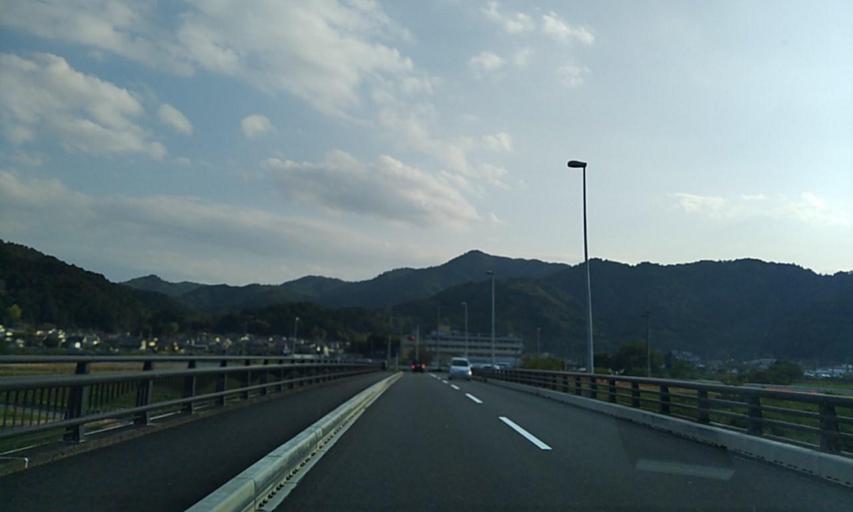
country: JP
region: Kyoto
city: Ayabe
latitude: 35.3075
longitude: 135.2047
